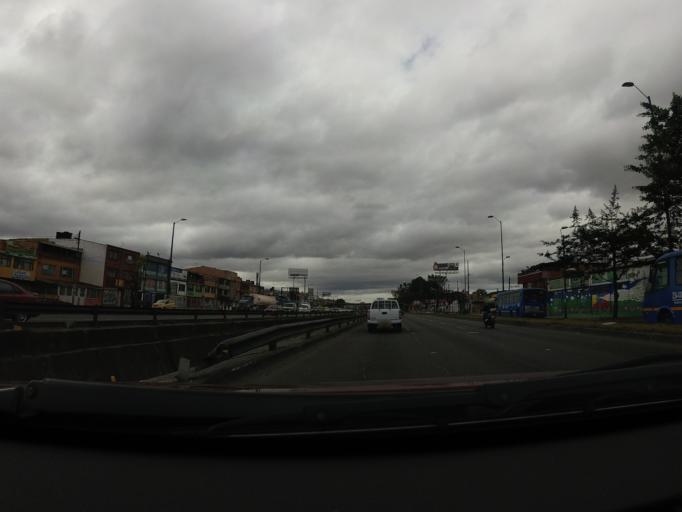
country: CO
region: Bogota D.C.
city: Bogota
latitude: 4.6810
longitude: -74.0995
